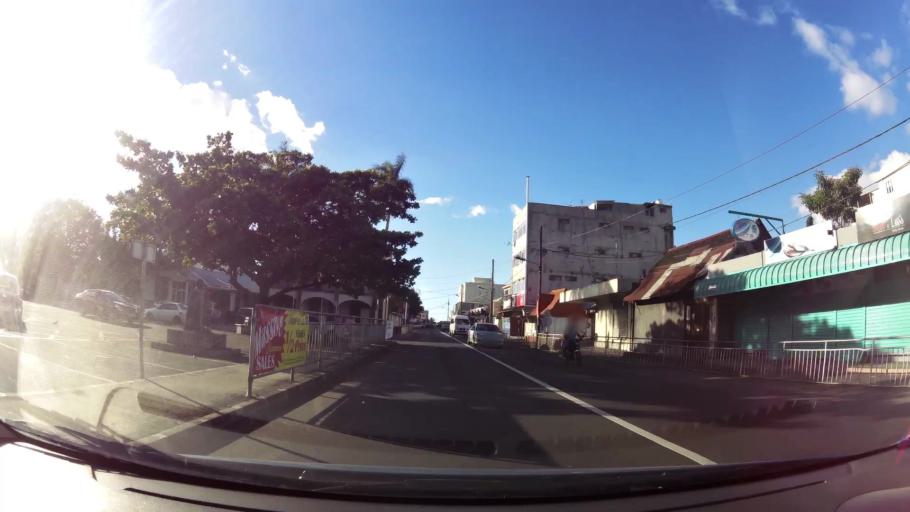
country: MU
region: Moka
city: Moka
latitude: -20.2266
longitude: 57.4679
